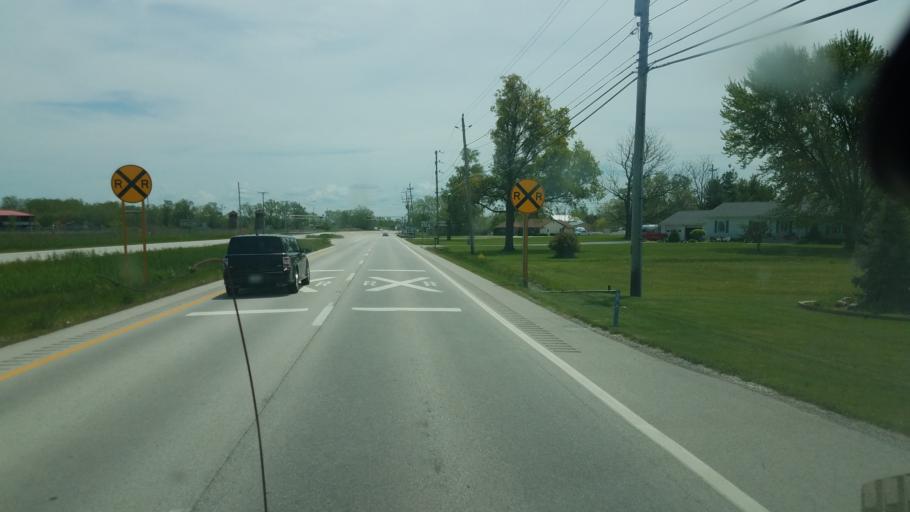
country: US
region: Ohio
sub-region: Ottawa County
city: Port Clinton
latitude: 41.5318
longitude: -83.0233
